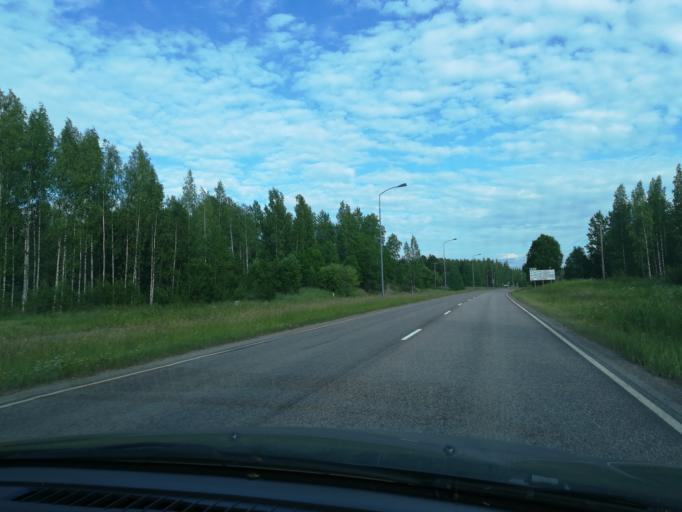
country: FI
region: South Karelia
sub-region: Imatra
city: Imatra
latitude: 61.1563
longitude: 28.7985
